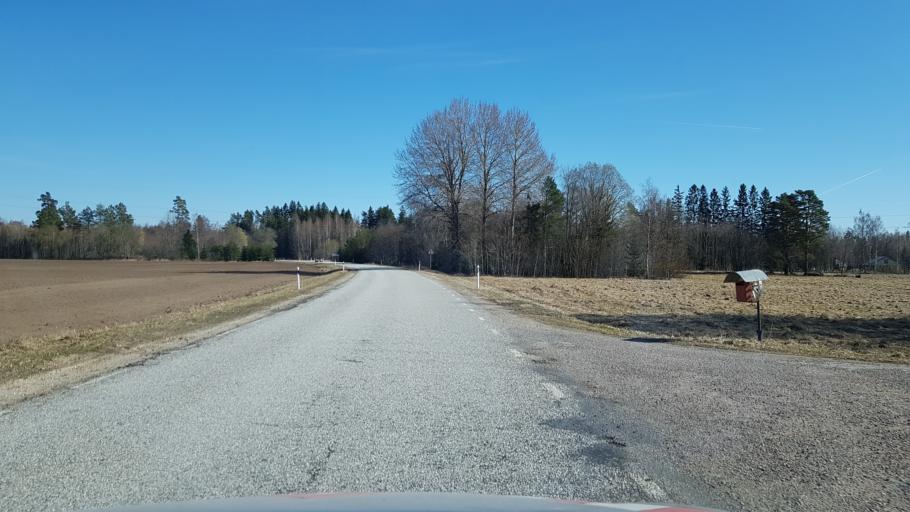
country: EE
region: Laeaene-Virumaa
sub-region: Vinni vald
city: Vinni
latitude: 59.2339
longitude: 26.6975
